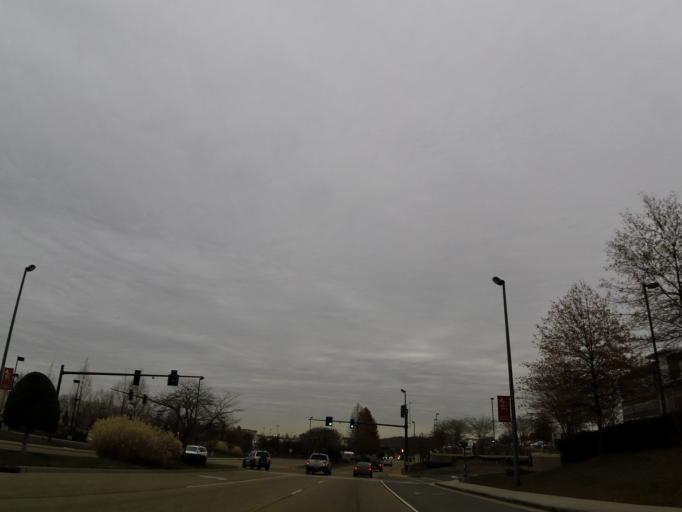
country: US
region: Tennessee
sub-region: Knox County
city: Farragut
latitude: 35.8994
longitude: -84.1641
